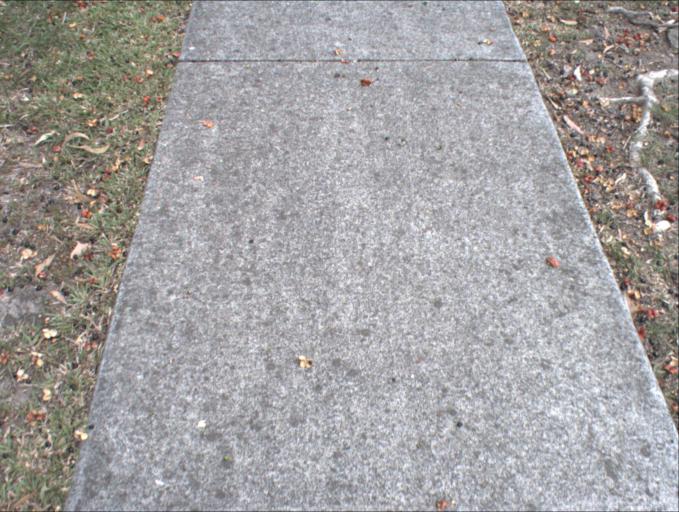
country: AU
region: Queensland
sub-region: Logan
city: Slacks Creek
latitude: -27.6517
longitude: 153.1903
